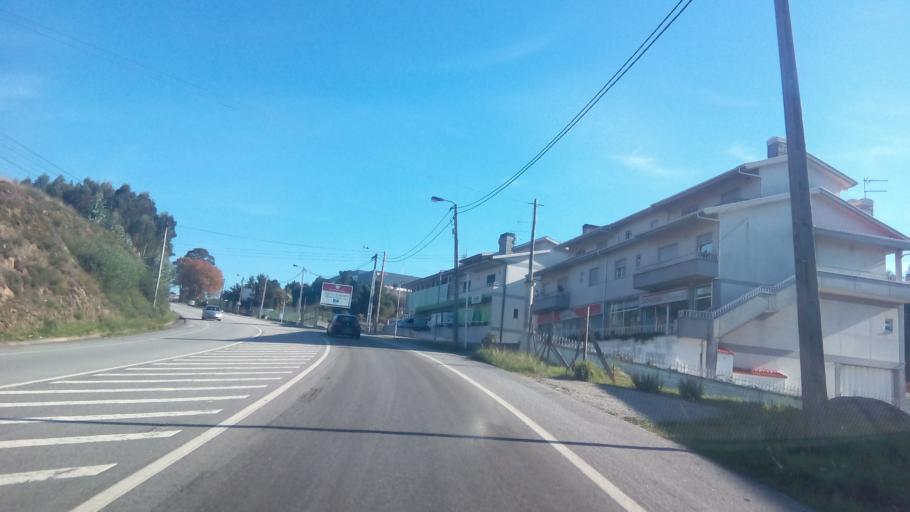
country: PT
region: Porto
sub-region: Paredes
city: Gandra
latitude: 41.1934
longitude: -8.4166
